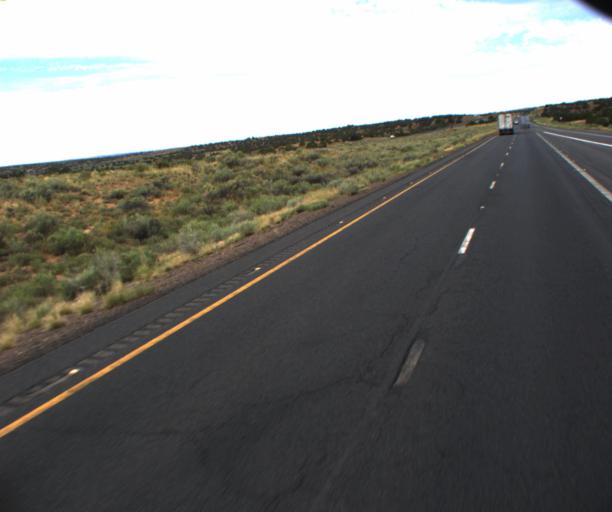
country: US
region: Arizona
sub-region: Apache County
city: Houck
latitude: 35.2815
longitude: -109.2433
